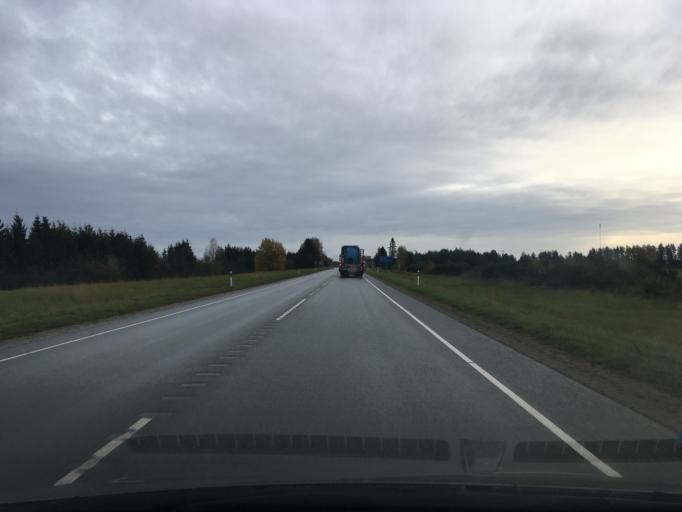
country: EE
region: Laeaene-Virumaa
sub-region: Viru-Nigula vald
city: Kunda
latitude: 59.4280
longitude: 26.6908
